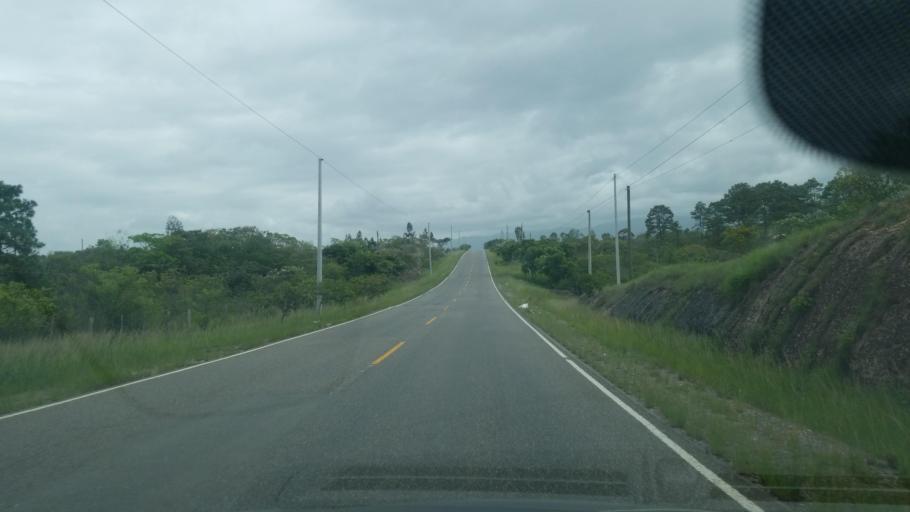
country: HN
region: Ocotepeque
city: Lucerna
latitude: 14.5350
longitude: -88.9488
